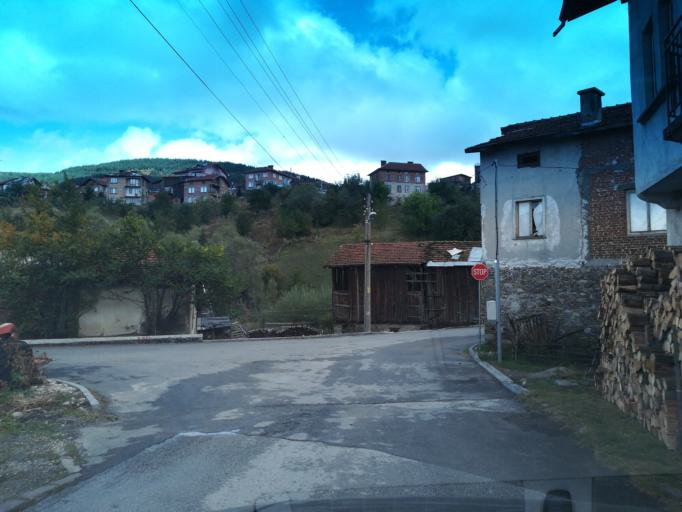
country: BG
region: Pazardzhik
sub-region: Obshtina Batak
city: Batak
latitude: 41.9369
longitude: 24.2681
